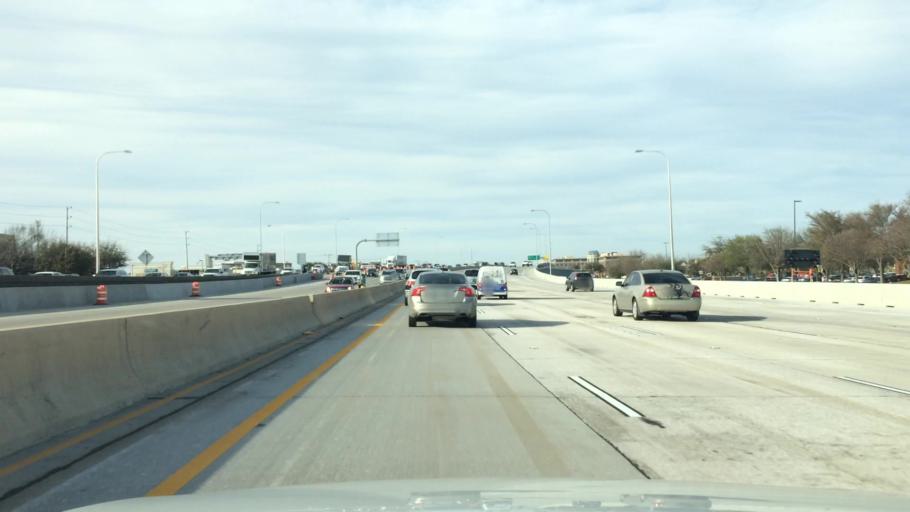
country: US
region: Texas
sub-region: Dallas County
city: Addison
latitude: 33.0236
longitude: -96.8298
